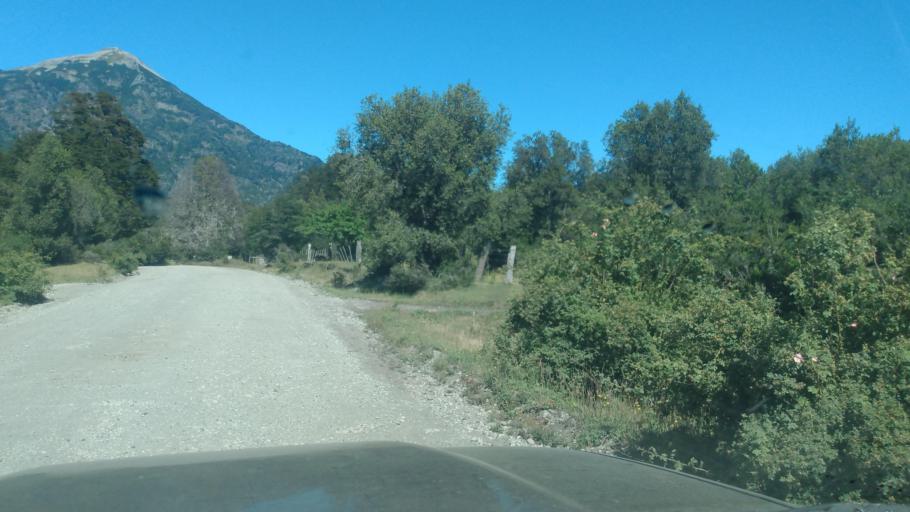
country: AR
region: Neuquen
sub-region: Departamento de Lacar
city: San Martin de los Andes
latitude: -39.7483
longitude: -71.4953
